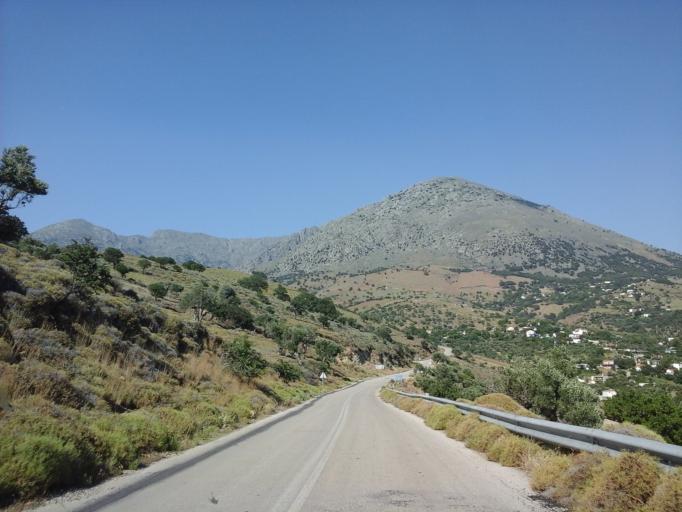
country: GR
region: East Macedonia and Thrace
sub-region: Nomos Evrou
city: Samothraki
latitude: 40.4282
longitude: 25.5222
